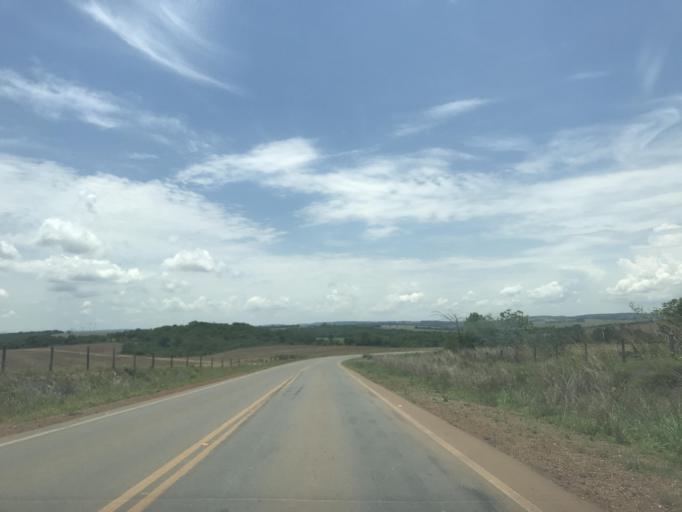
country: BR
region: Goias
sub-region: Vianopolis
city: Vianopolis
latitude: -16.6331
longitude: -48.3555
